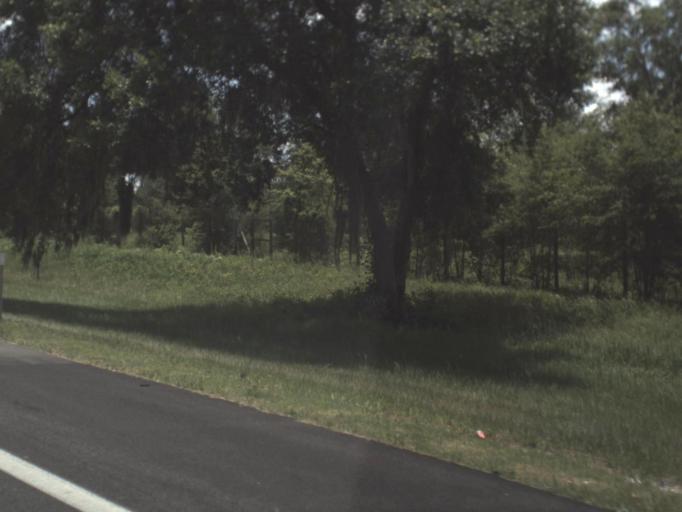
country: US
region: Florida
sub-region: Madison County
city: Madison
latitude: 30.3945
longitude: -83.3497
